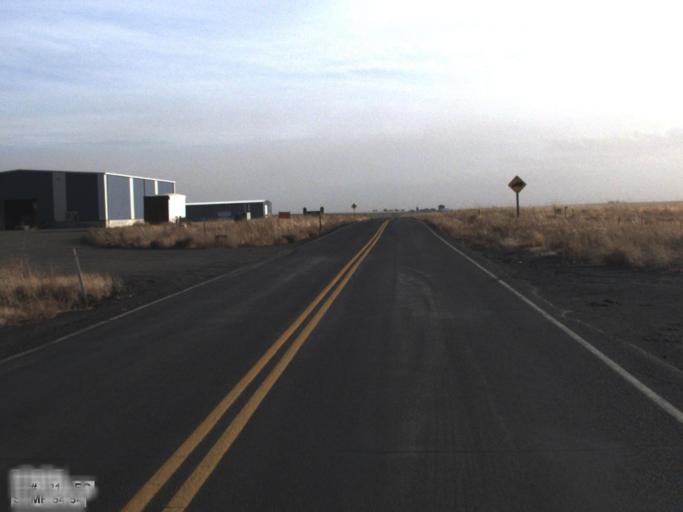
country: US
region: Washington
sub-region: Adams County
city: Ritzville
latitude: 47.3189
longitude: -118.6904
